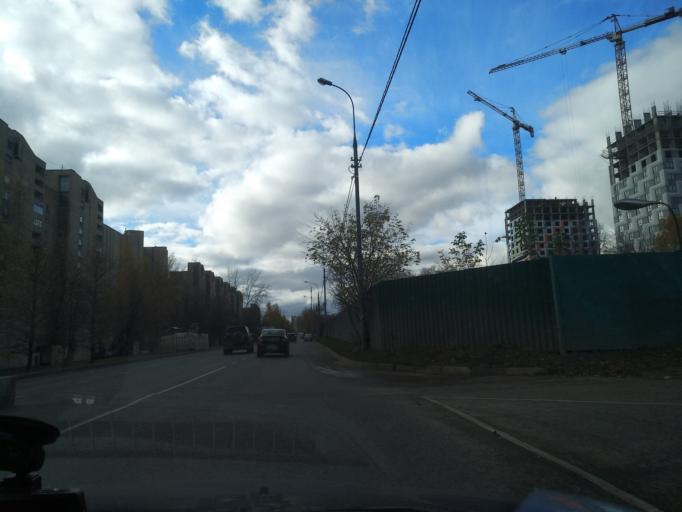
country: RU
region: Moscow
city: Otradnoye
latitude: 55.8746
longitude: 37.6064
